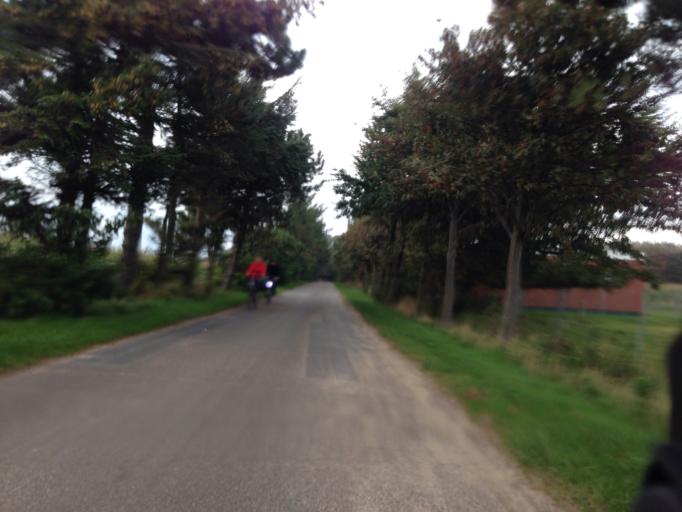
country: DE
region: Schleswig-Holstein
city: Nieblum
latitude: 54.6840
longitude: 8.4854
